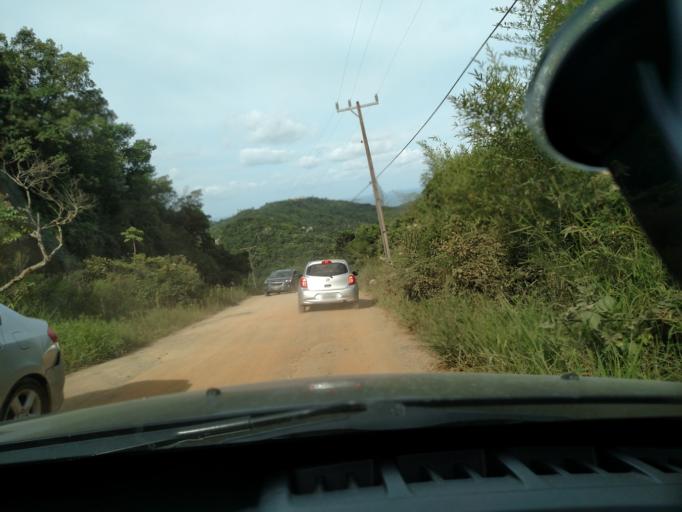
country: BR
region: Santa Catarina
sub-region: Porto Belo
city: Porto Belo
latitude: -27.2090
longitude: -48.4965
